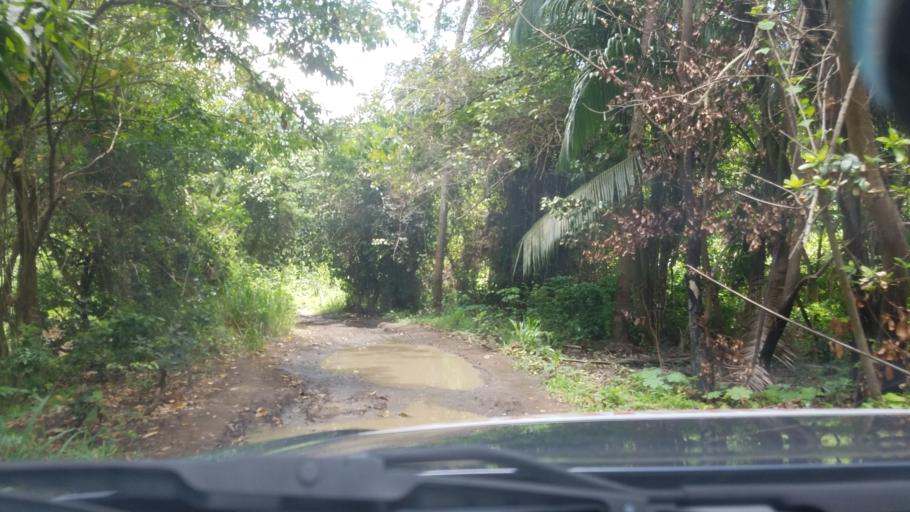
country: LC
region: Gros-Islet
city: Gros Islet
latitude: 14.0568
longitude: -60.9274
